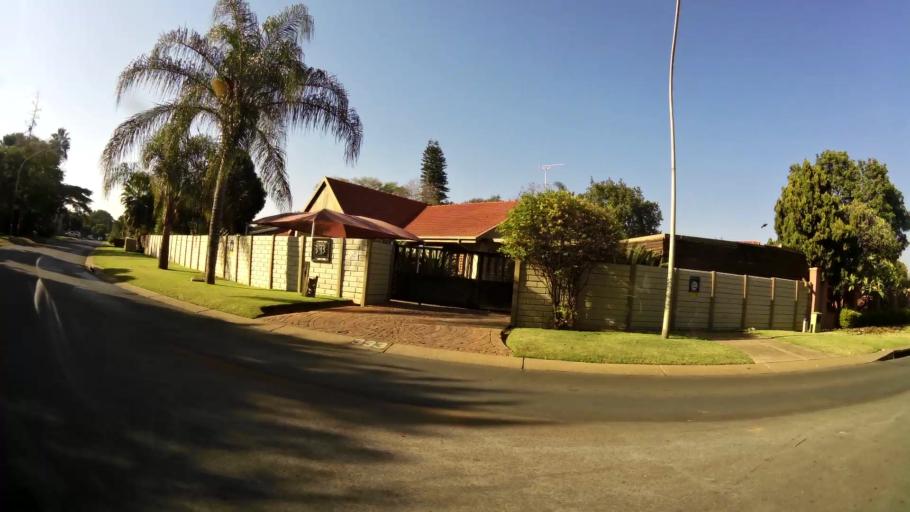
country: ZA
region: Gauteng
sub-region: City of Tshwane Metropolitan Municipality
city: Pretoria
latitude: -25.6764
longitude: 28.2313
